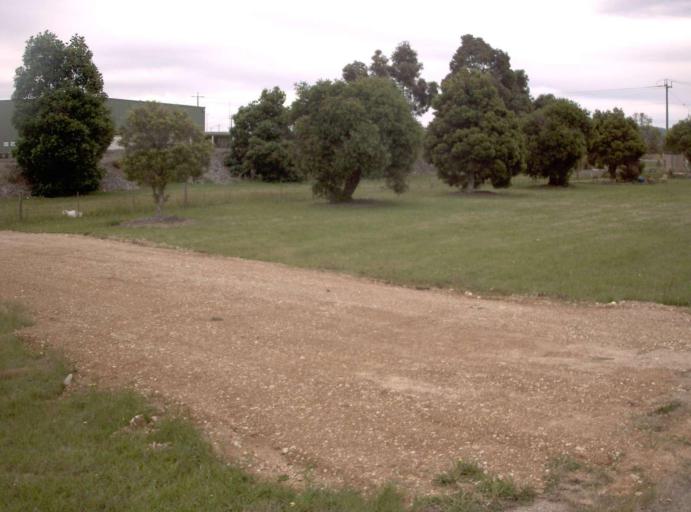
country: AU
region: Victoria
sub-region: East Gippsland
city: Bairnsdale
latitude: -37.8467
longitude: 147.5665
